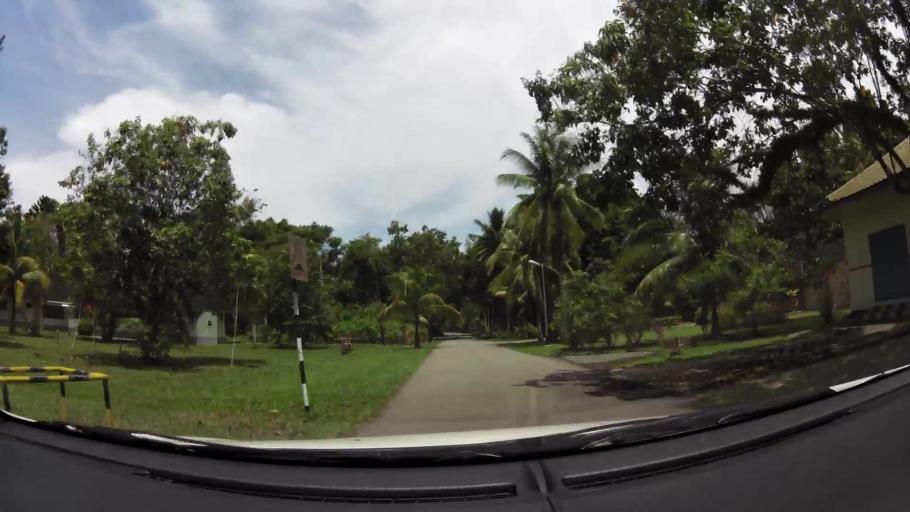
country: BN
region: Belait
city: Kuala Belait
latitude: 4.5951
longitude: 114.2606
